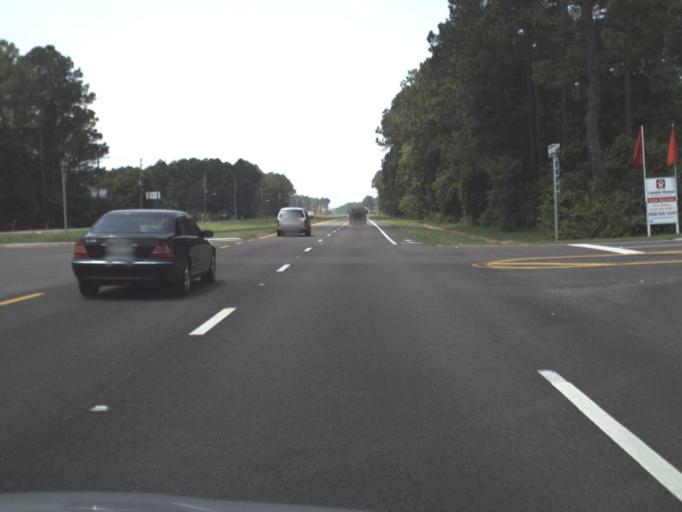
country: US
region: Florida
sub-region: Duval County
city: Baldwin
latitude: 30.2652
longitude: -81.8537
